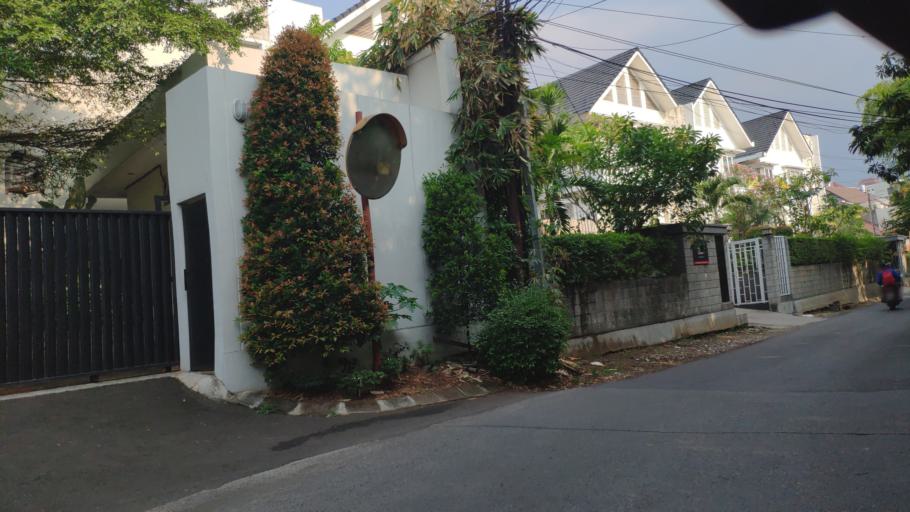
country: ID
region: Banten
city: South Tangerang
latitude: -6.2863
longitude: 106.8004
